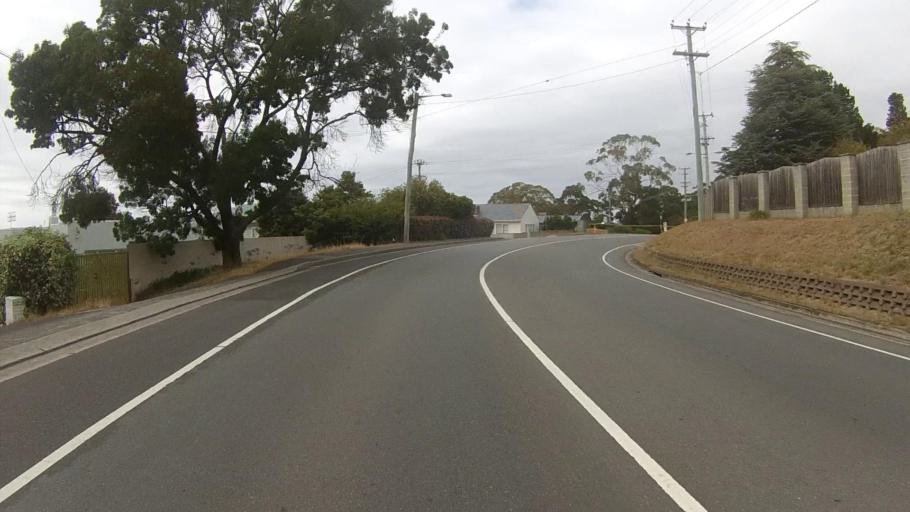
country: AU
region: Tasmania
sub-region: Kingborough
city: Taroona
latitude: -42.9356
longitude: 147.3543
